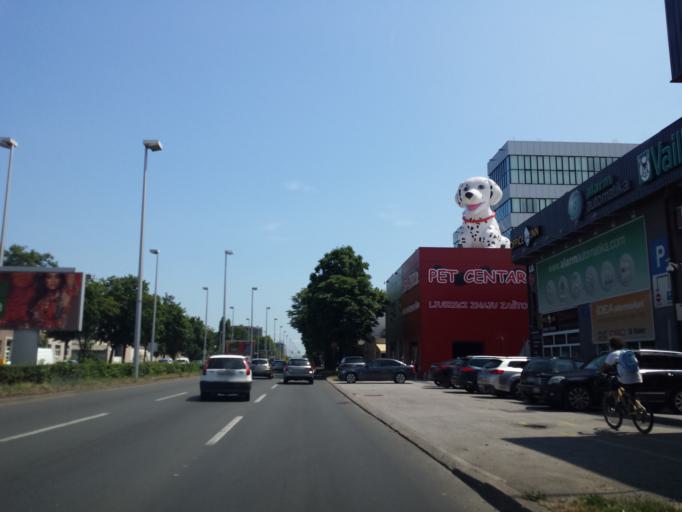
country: HR
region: Grad Zagreb
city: Zagreb
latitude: 45.8086
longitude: 16.0037
